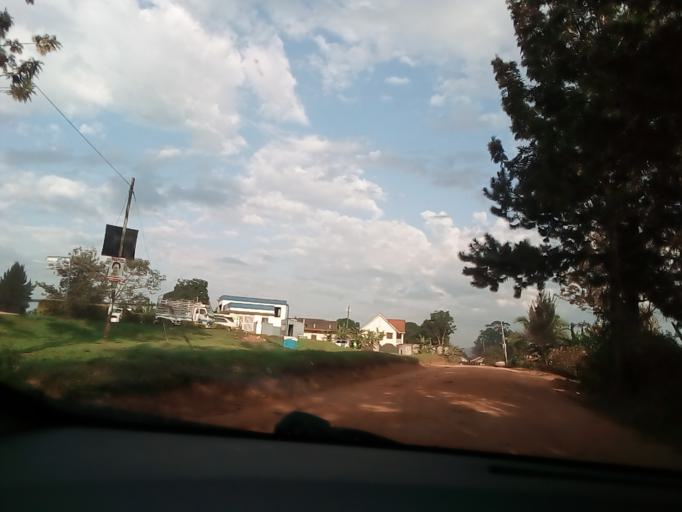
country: UG
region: Central Region
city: Masaka
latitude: -0.3435
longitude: 31.7296
